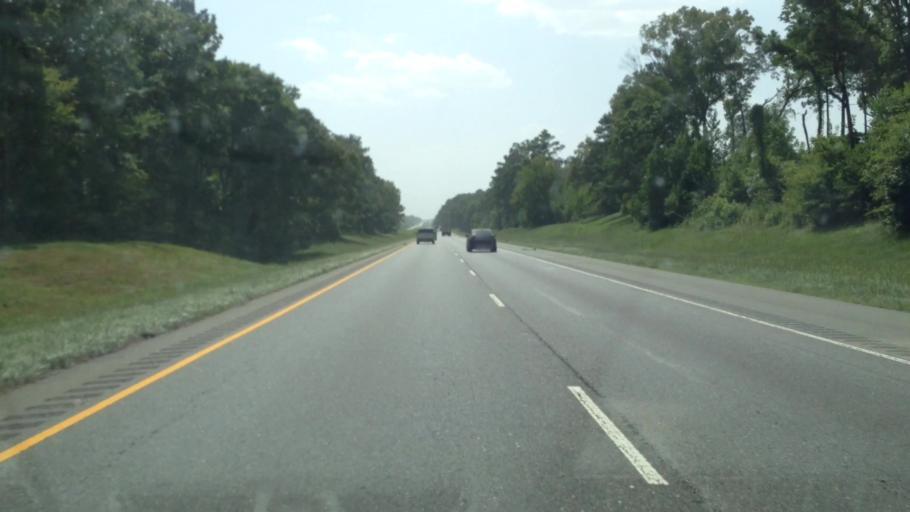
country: US
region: Louisiana
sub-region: Bossier Parish
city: Eastwood
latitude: 32.5423
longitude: -93.5626
